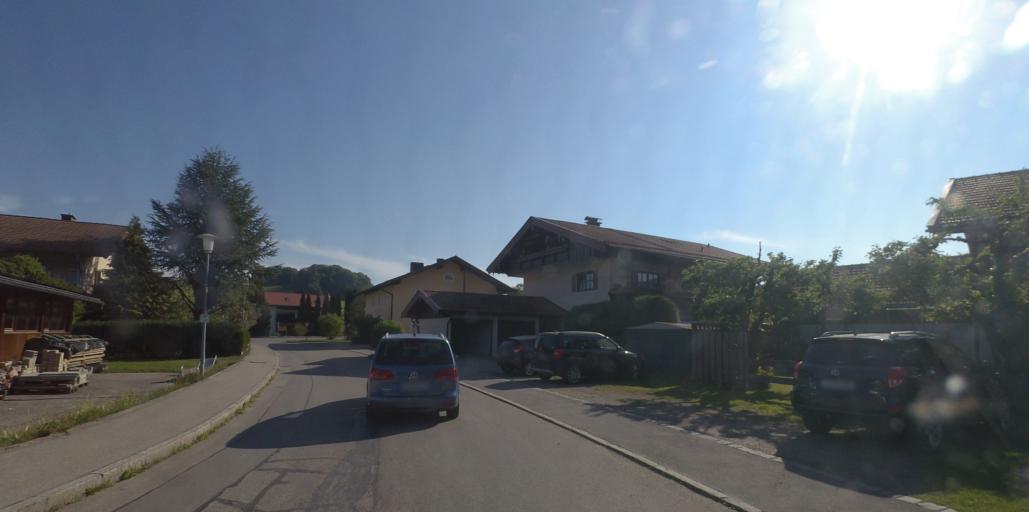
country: DE
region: Bavaria
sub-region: Upper Bavaria
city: Vachendorf
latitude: 47.8431
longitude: 12.6067
